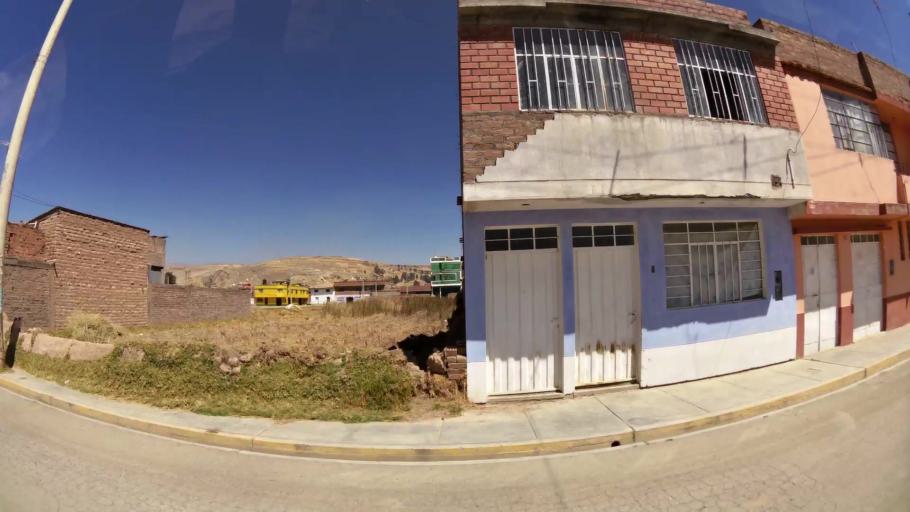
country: PE
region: Junin
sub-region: Provincia de Jauja
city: Jauja
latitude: -11.7726
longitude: -75.4934
